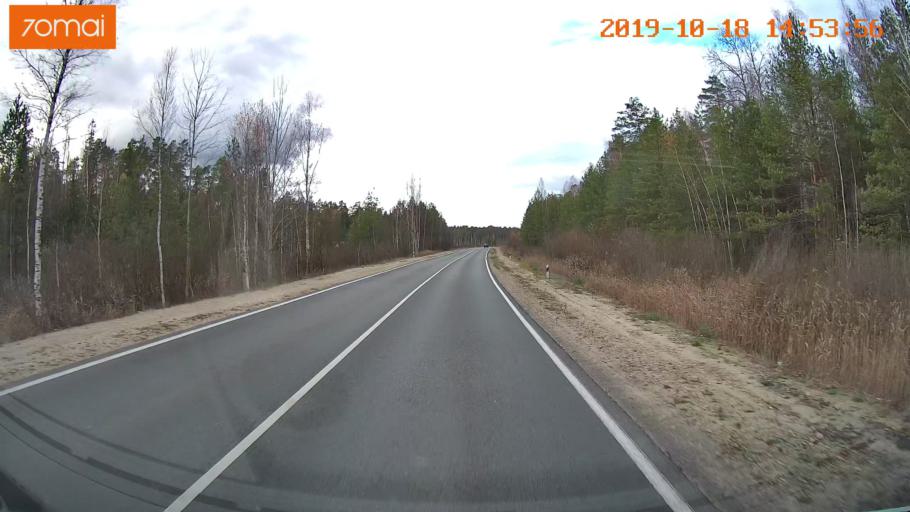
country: RU
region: Vladimir
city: Kurlovo
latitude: 55.4352
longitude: 40.6075
